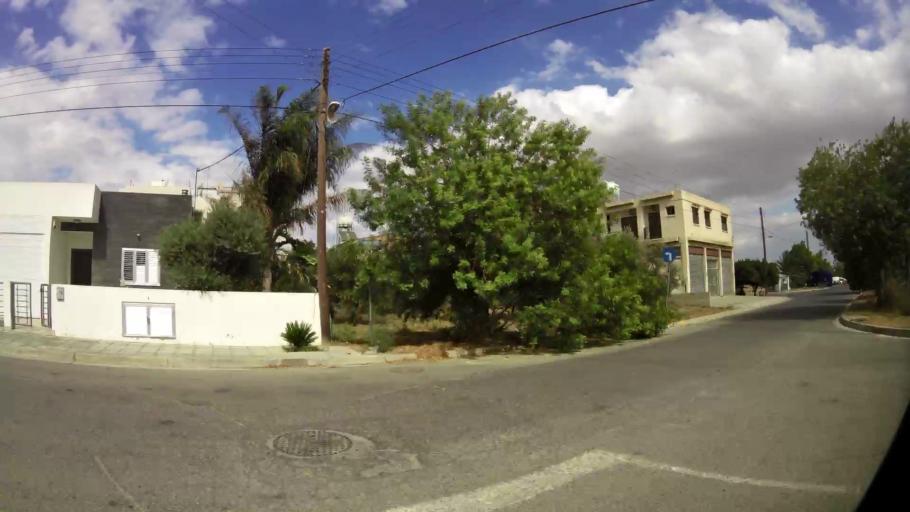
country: CY
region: Lefkosia
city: Nicosia
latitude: 35.1870
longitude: 33.3953
